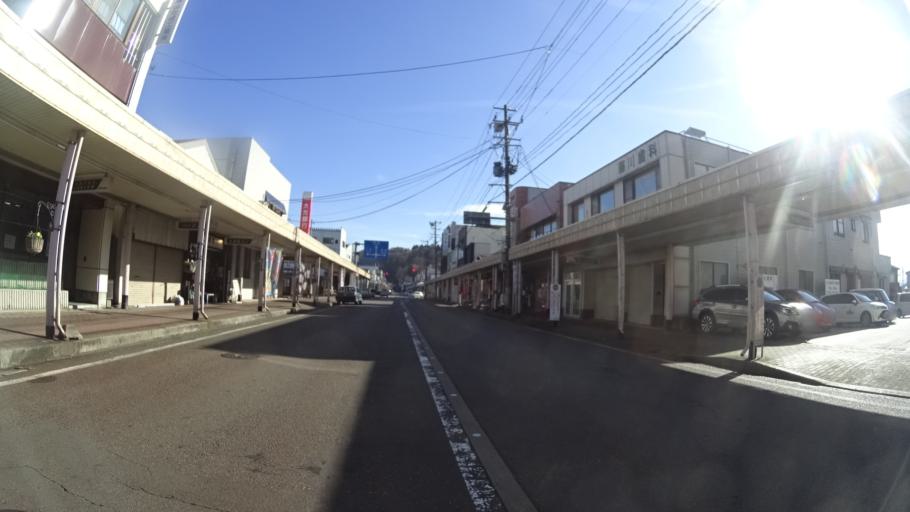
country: JP
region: Niigata
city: Mitsuke
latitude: 37.5271
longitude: 138.9231
